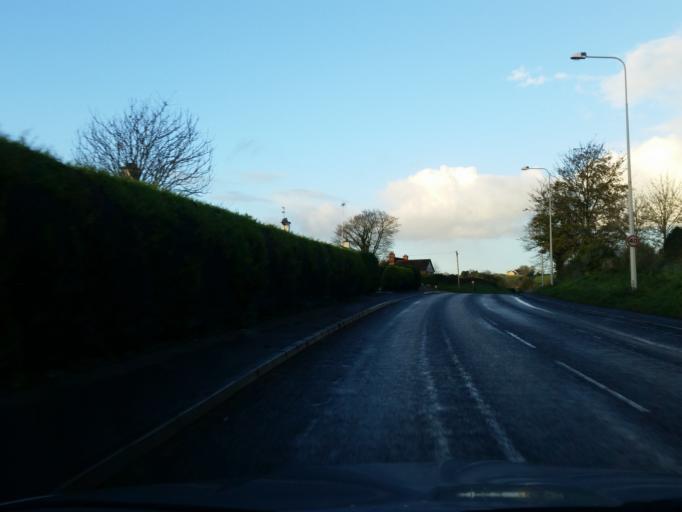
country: GB
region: Northern Ireland
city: Lisnaskea
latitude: 54.2483
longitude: -7.4480
